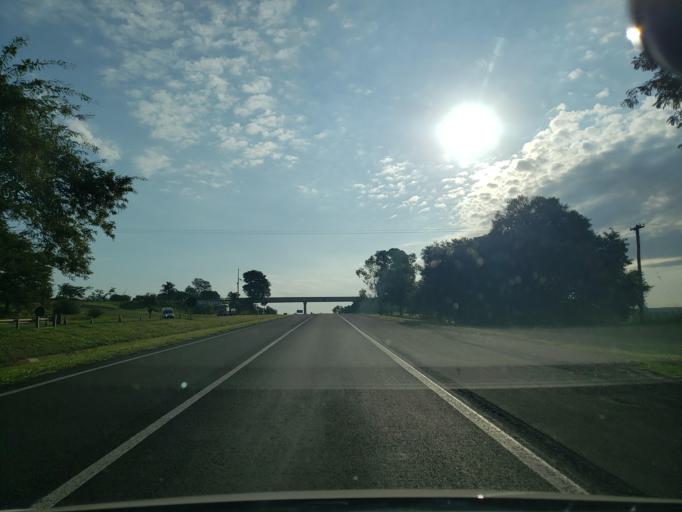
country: BR
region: Sao Paulo
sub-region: Valparaiso
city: Valparaiso
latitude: -21.2129
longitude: -50.8641
